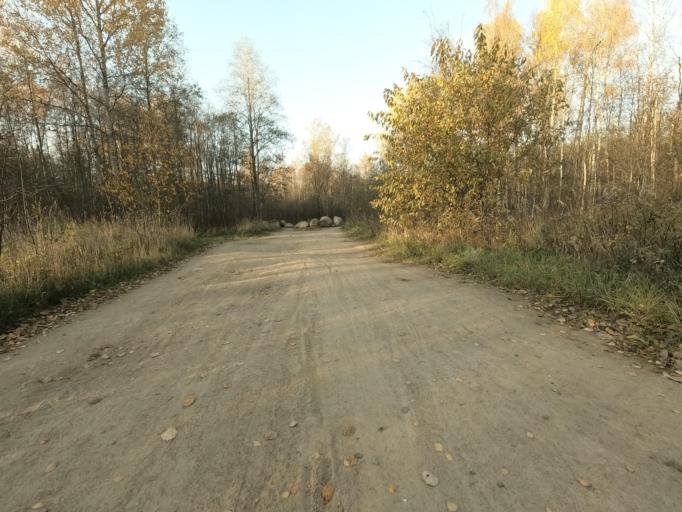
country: RU
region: Leningrad
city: Sinyavino
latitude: 59.8772
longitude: 31.0402
